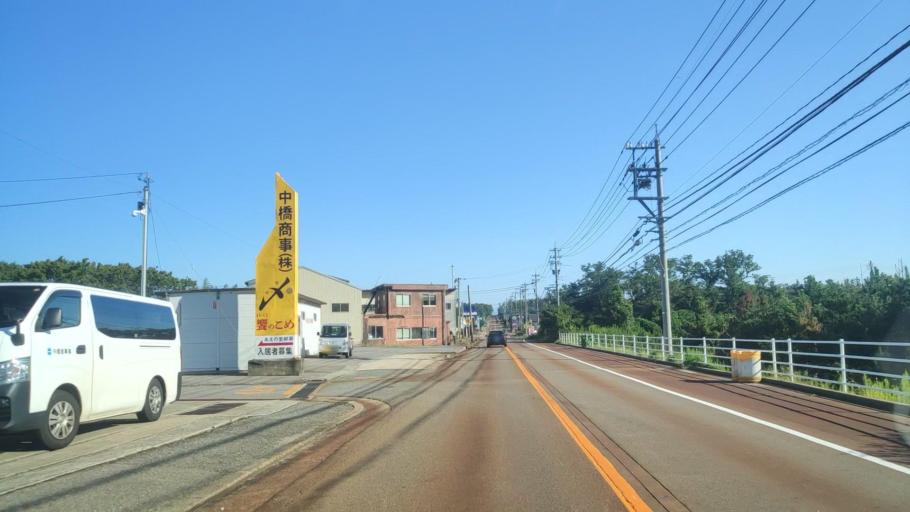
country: JP
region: Ishikawa
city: Hakui
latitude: 36.8601
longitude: 136.7701
